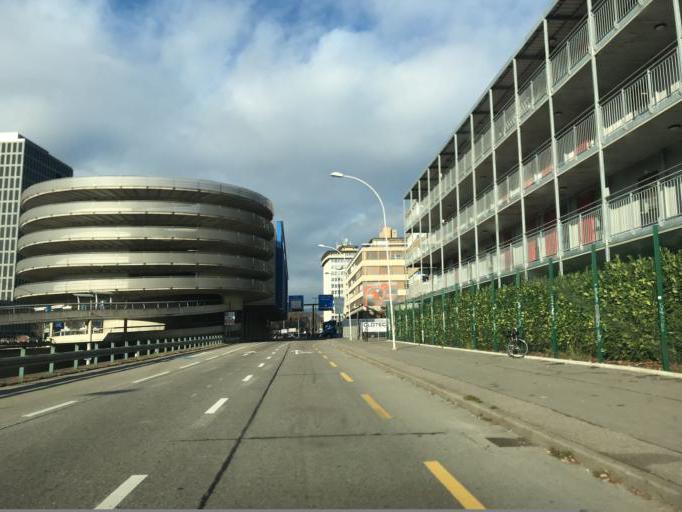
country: CH
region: Geneva
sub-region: Geneva
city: Carouge
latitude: 46.1857
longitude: 6.1286
